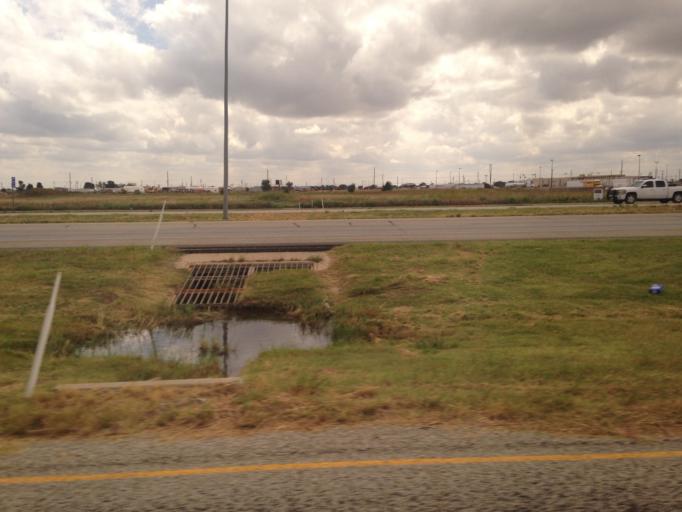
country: US
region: Texas
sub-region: Lubbock County
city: Lubbock
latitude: 33.5319
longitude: -101.8063
